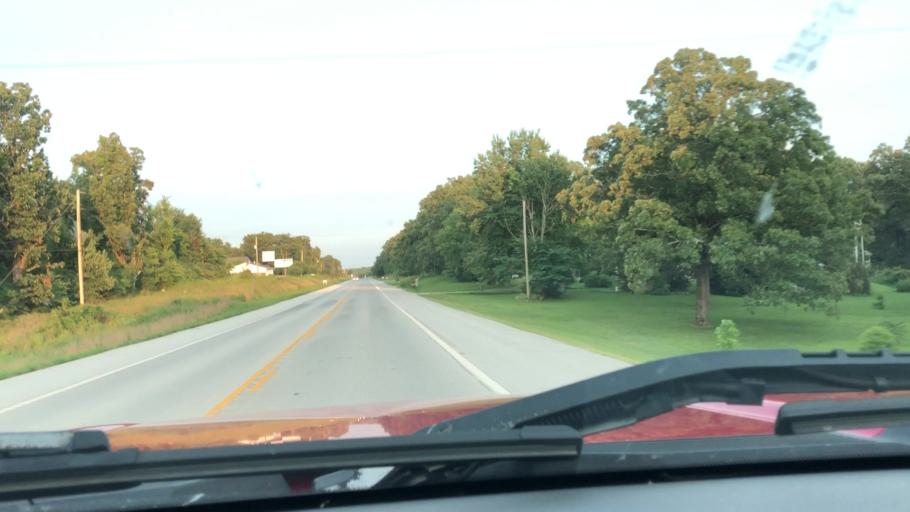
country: US
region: Missouri
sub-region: Jasper County
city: Duquesne
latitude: 36.9743
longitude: -94.4568
